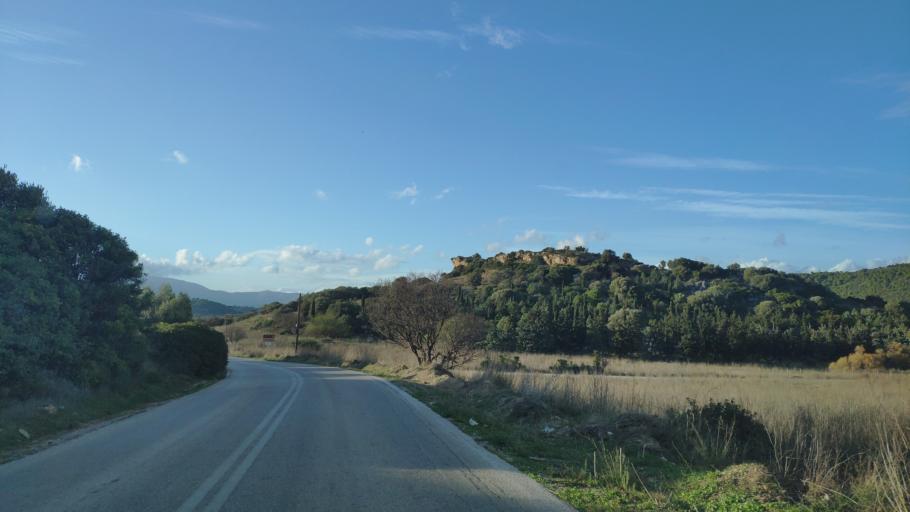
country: GR
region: Attica
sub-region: Nomarchia Anatolikis Attikis
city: Limin Mesoyaias
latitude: 37.9221
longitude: 23.9979
